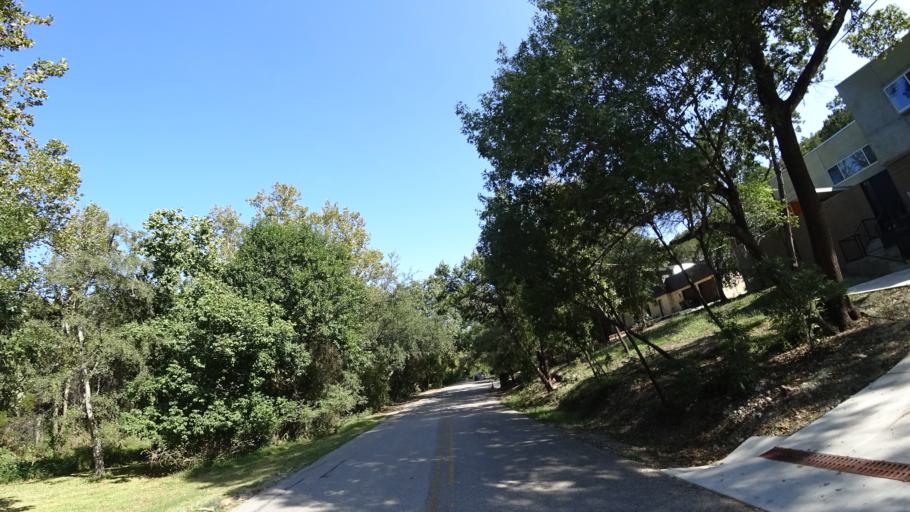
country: US
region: Texas
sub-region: Travis County
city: West Lake Hills
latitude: 30.2938
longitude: -97.8051
